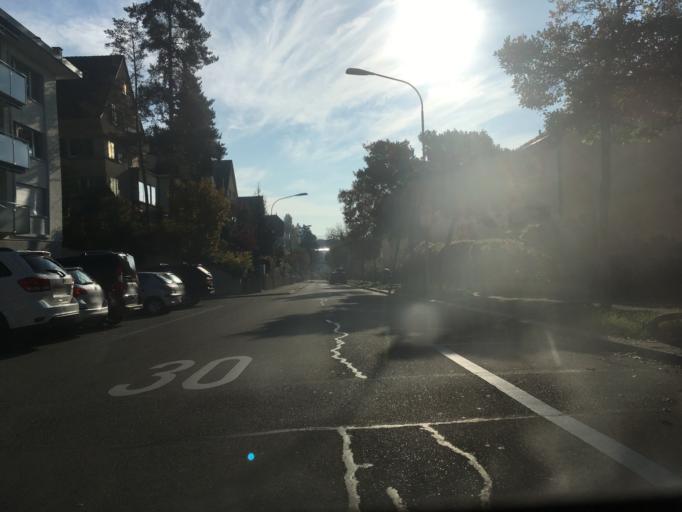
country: CH
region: Zurich
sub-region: Bezirk Zuerich
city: Zuerich (Kreis 10) / Hoengg
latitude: 47.4005
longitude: 8.5007
